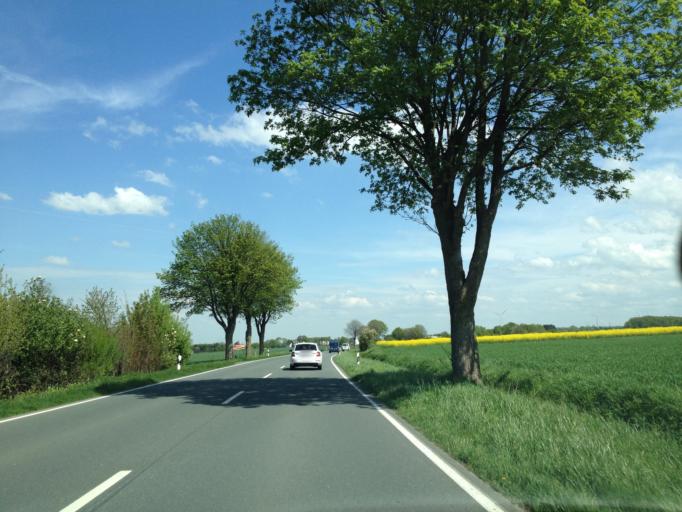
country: DE
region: North Rhine-Westphalia
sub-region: Regierungsbezirk Arnsberg
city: Mohnesee
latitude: 51.5055
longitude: 8.0529
